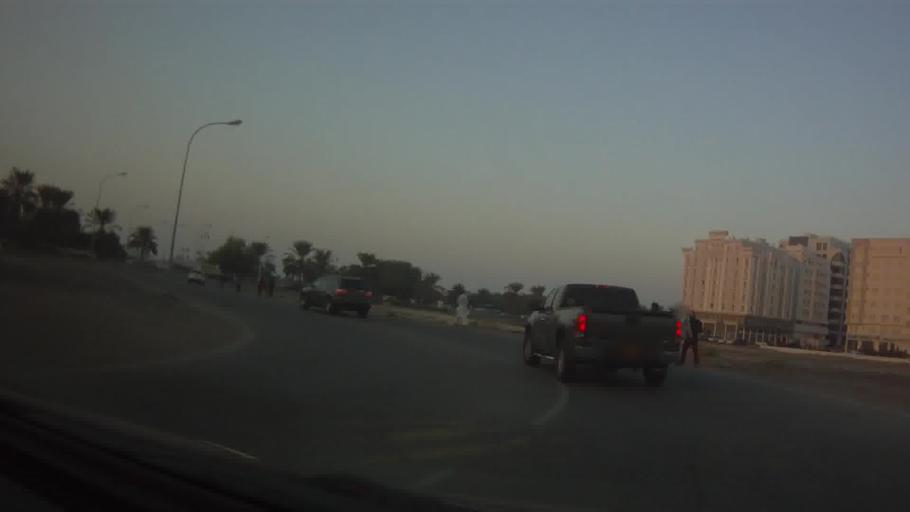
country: OM
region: Muhafazat Masqat
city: Bawshar
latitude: 23.5950
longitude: 58.4136
